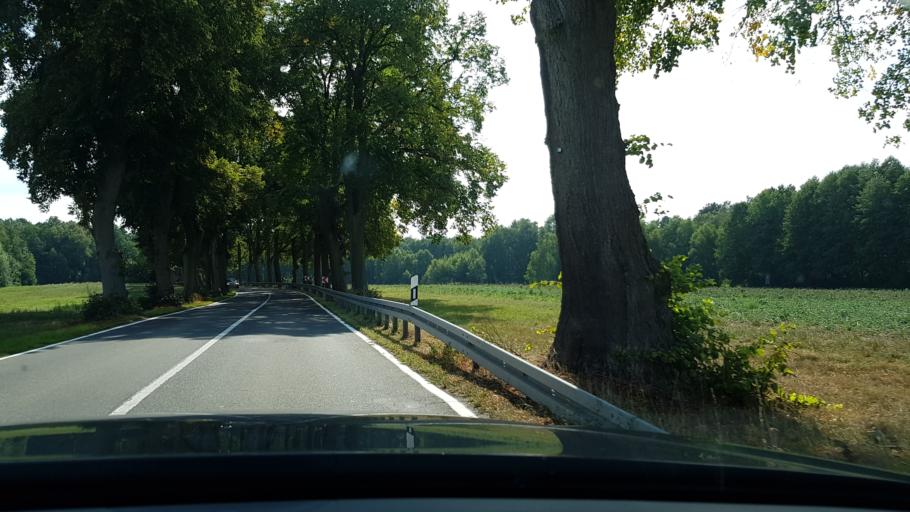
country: DE
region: Brandenburg
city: Lindow
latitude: 53.0135
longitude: 12.9786
